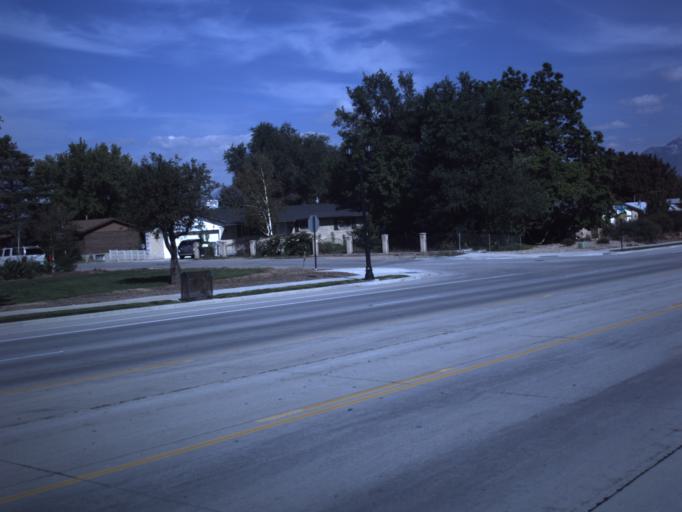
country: US
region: Utah
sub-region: Salt Lake County
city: South Jordan Heights
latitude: 40.5621
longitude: -111.9630
